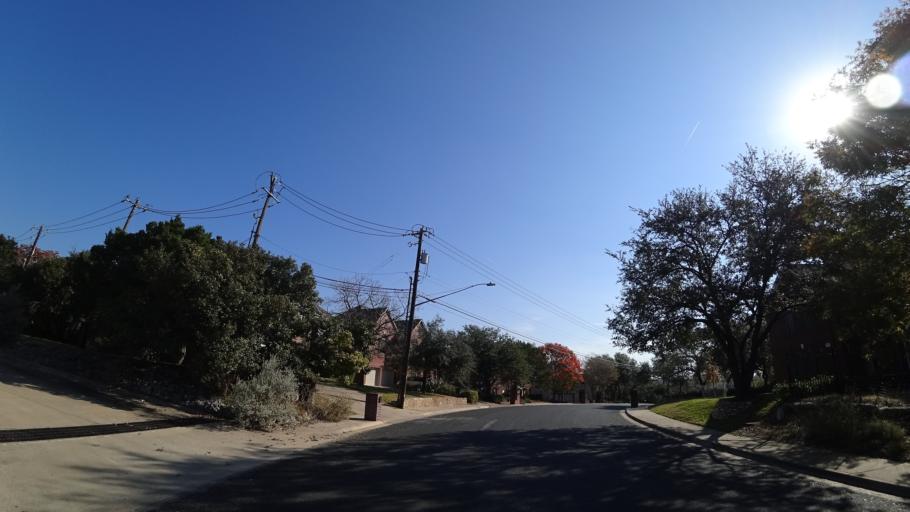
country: US
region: Texas
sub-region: Williamson County
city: Jollyville
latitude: 30.3985
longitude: -97.7673
